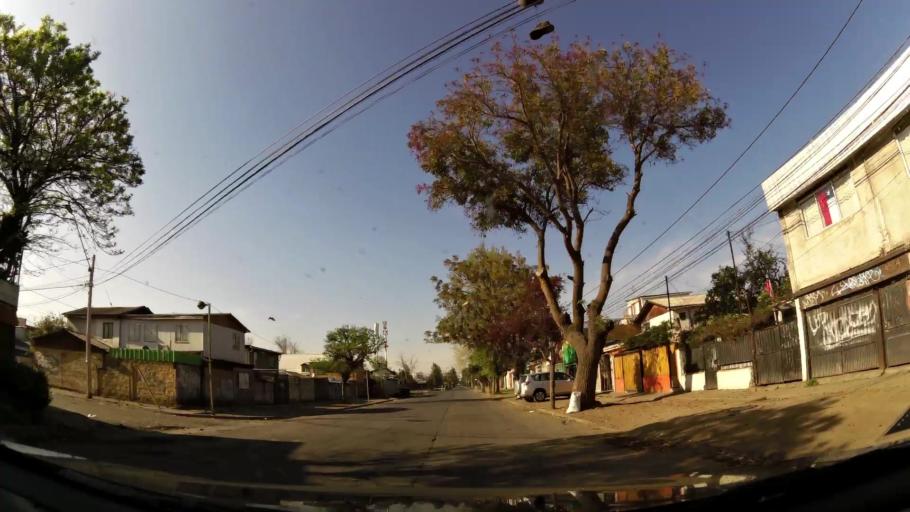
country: CL
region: Santiago Metropolitan
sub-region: Provincia de Santiago
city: Santiago
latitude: -33.3853
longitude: -70.6672
